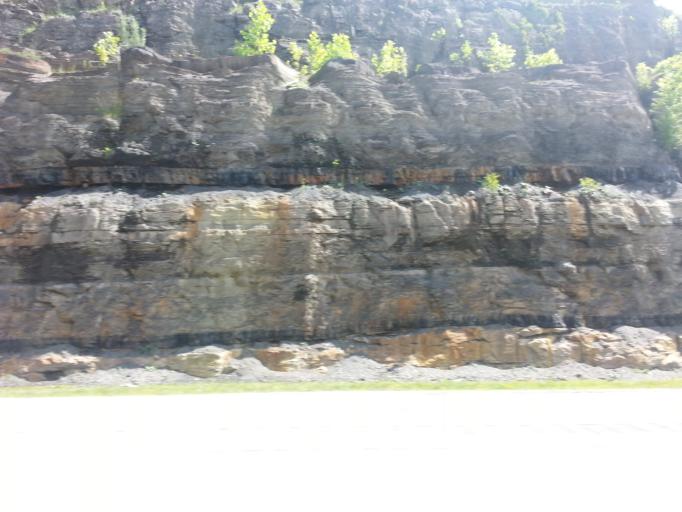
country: US
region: Kentucky
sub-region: Harlan County
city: Harlan
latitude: 36.7817
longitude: -83.2342
